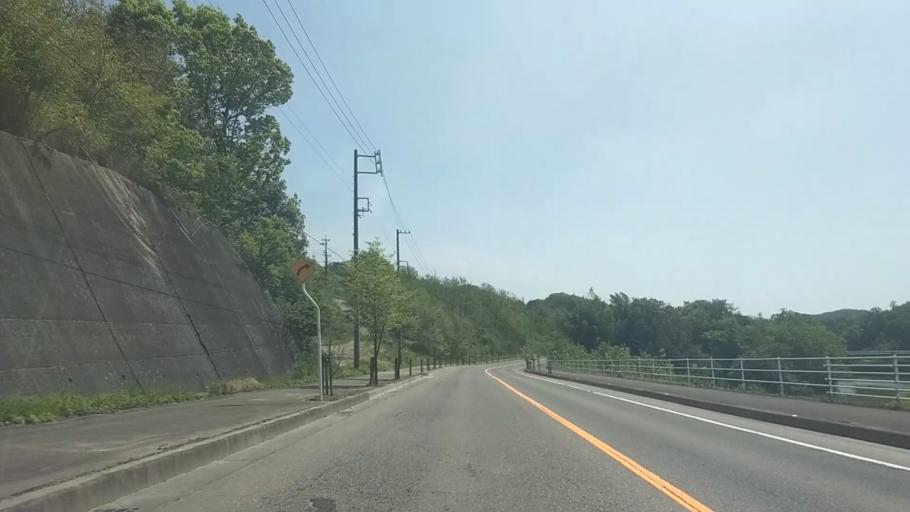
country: JP
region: Aichi
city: Okazaki
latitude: 34.9738
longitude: 137.1968
